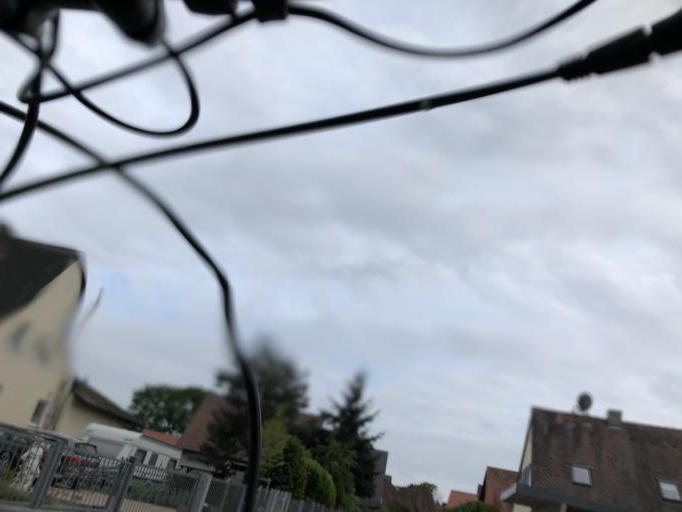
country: DE
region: Bavaria
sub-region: Regierungsbezirk Mittelfranken
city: Erlangen
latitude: 49.5351
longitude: 11.0252
